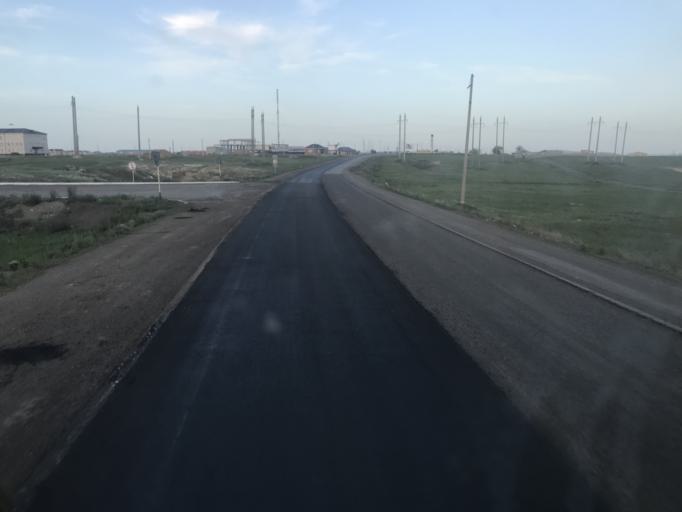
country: KZ
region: Aqtoebe
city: Khromtau
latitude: 50.2593
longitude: 58.4057
